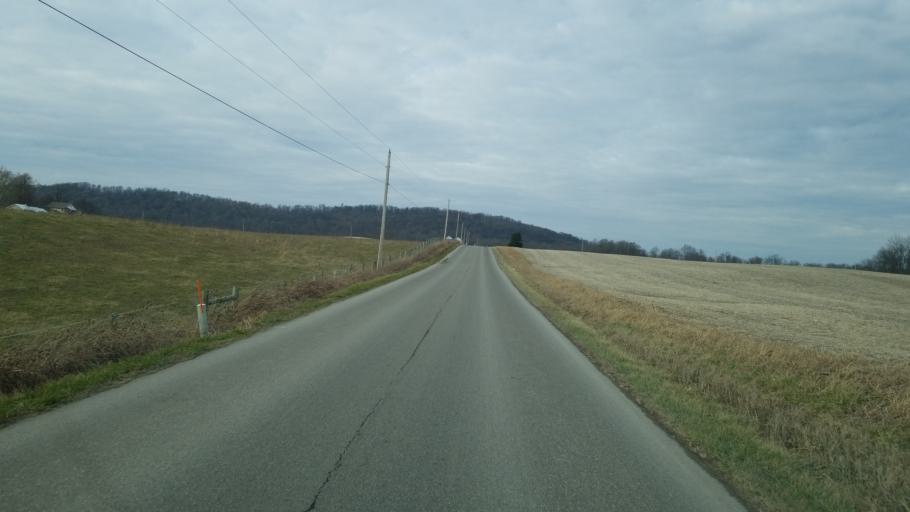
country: US
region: Ohio
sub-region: Highland County
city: Greenfield
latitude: 39.1915
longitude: -83.3162
